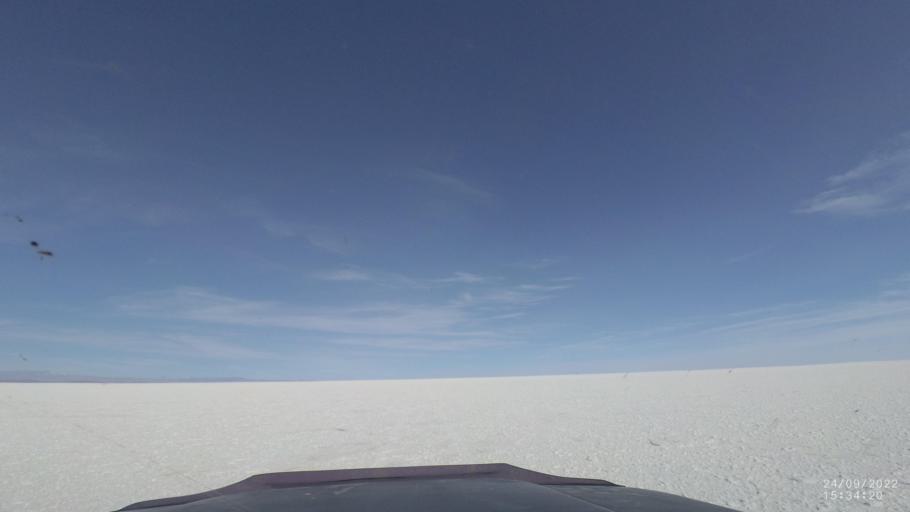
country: BO
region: Potosi
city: Colchani
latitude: -20.1236
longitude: -67.2634
